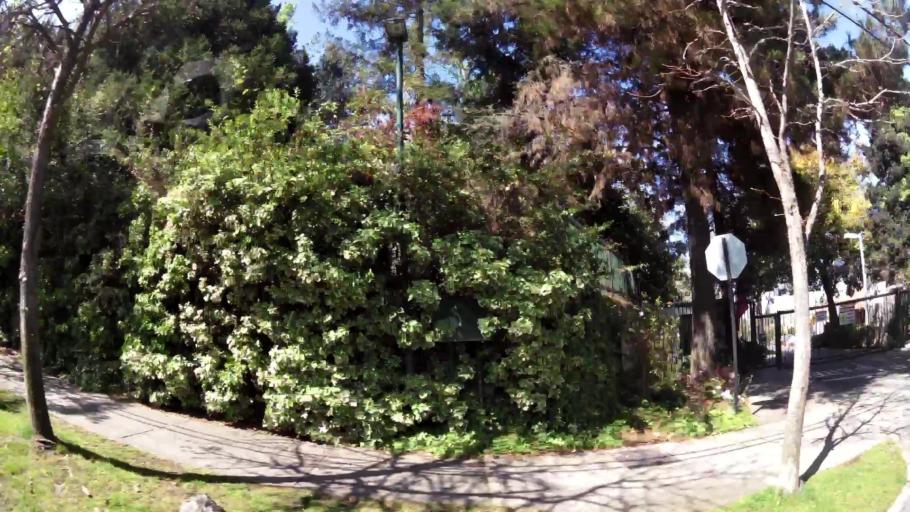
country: CL
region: Santiago Metropolitan
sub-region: Provincia de Santiago
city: Villa Presidente Frei, Nunoa, Santiago, Chile
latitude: -33.4375
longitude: -70.5277
